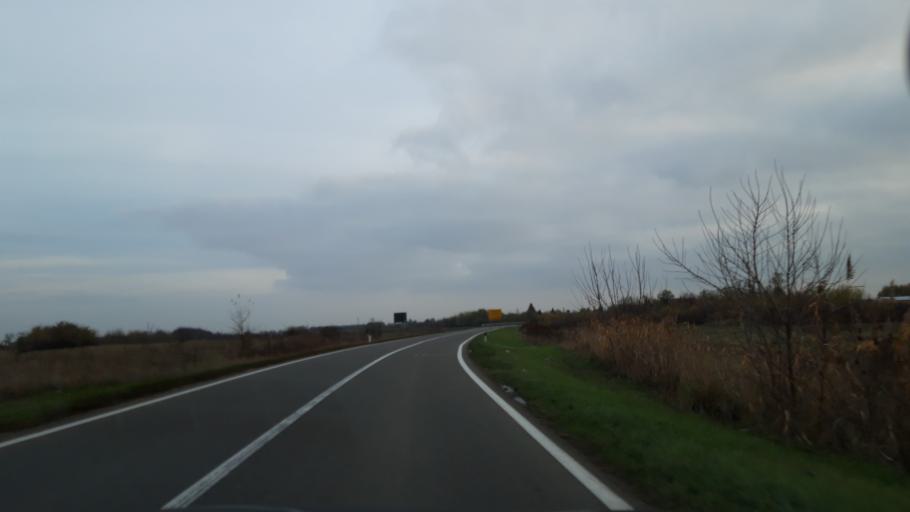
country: RS
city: Sanad
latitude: 45.9880
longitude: 20.1104
